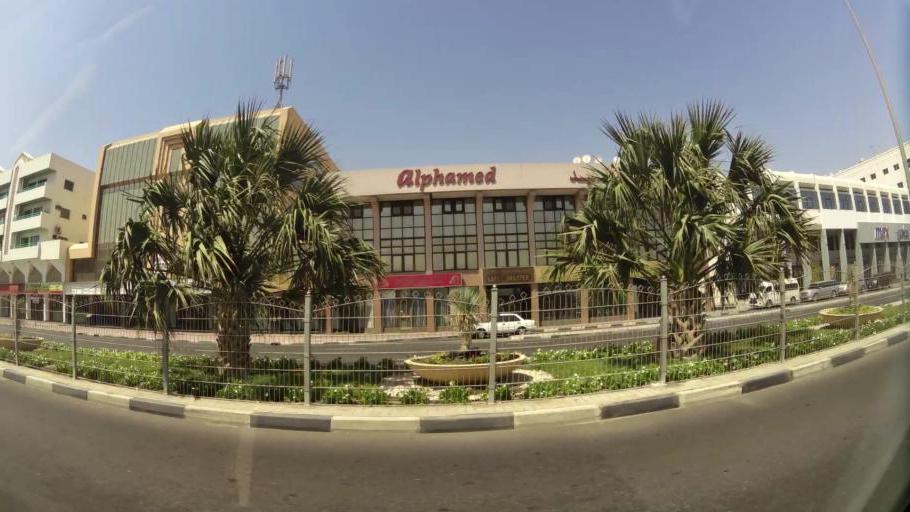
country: AE
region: Ash Shariqah
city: Sharjah
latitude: 25.2792
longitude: 55.3446
